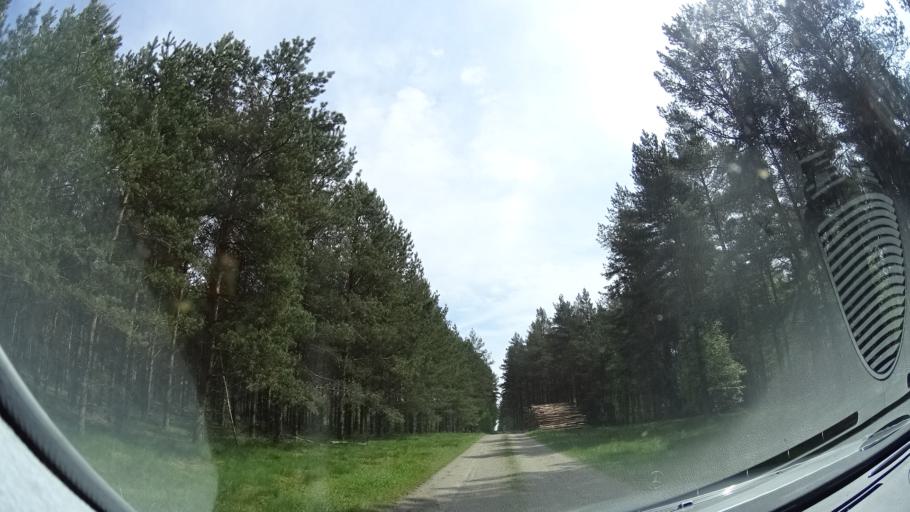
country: SE
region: Skane
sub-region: Sjobo Kommun
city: Sjoebo
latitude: 55.6698
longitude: 13.6409
